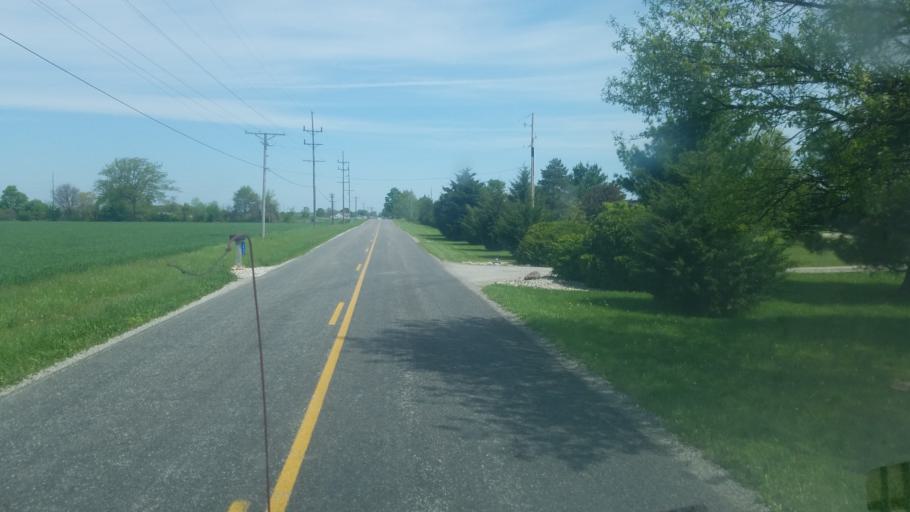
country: US
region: Ohio
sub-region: Seneca County
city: Tiffin
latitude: 41.1038
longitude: -83.1313
